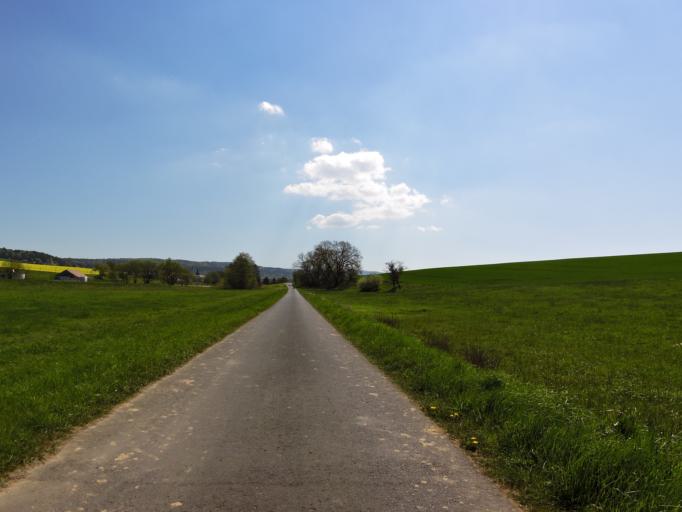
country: DE
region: Thuringia
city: Marksuhl
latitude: 50.9153
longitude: 10.1855
